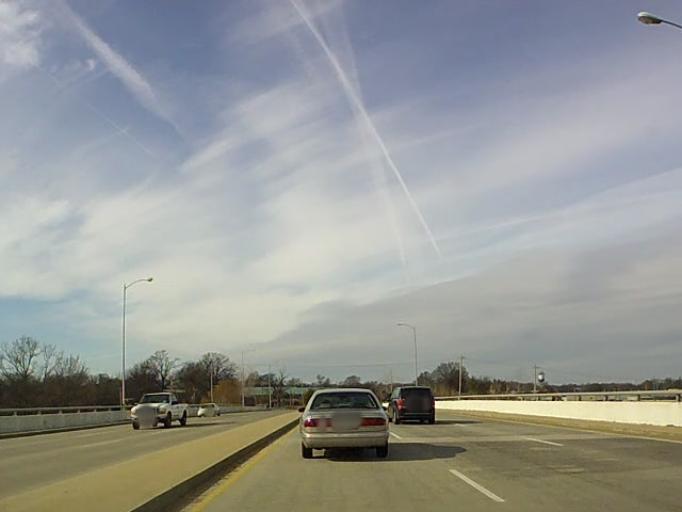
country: US
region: Tennessee
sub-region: Shelby County
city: Memphis
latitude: 35.1461
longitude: -89.9694
